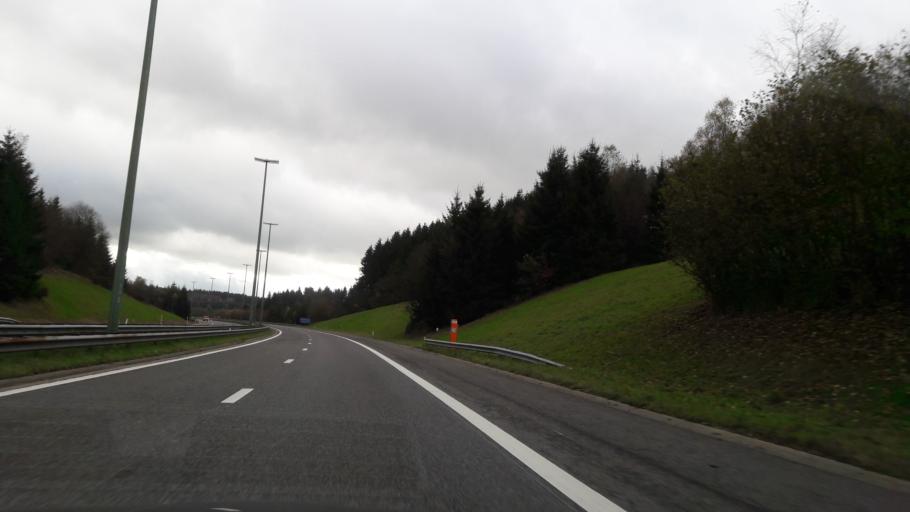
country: BE
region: Wallonia
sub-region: Province de Liege
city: Saint-Vith
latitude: 50.3056
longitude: 6.0791
